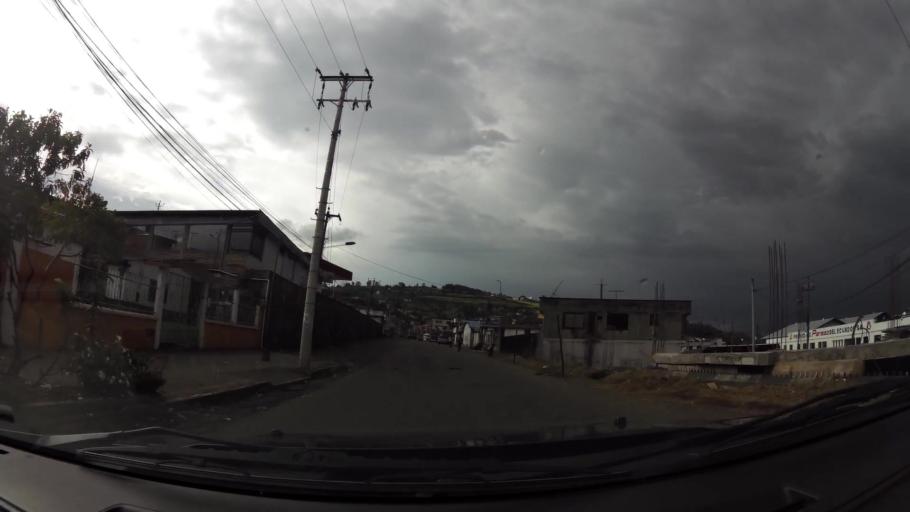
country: EC
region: Pichincha
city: Machachi
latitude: -0.4088
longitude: -78.5467
